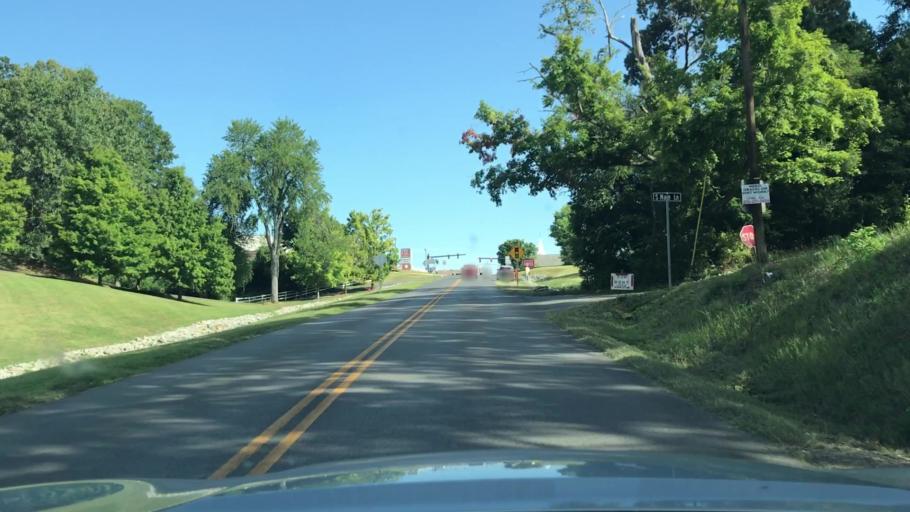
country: US
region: Kentucky
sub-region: Muhlenberg County
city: Greenville
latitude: 37.1970
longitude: -87.1772
